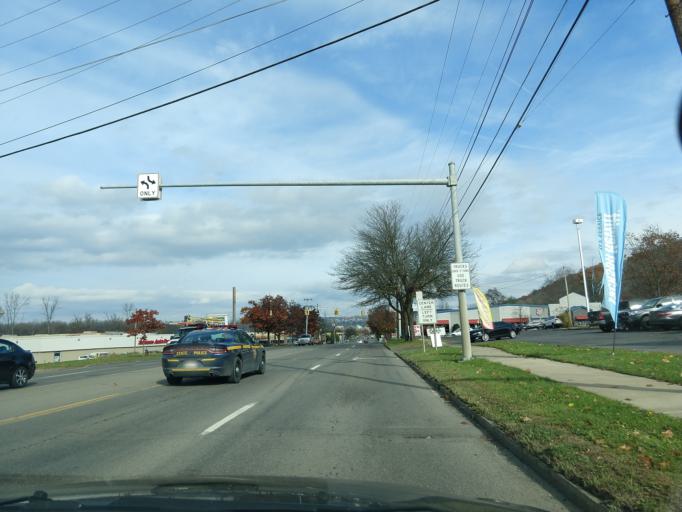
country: US
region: New York
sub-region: Tompkins County
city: South Hill
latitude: 42.4195
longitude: -76.5200
